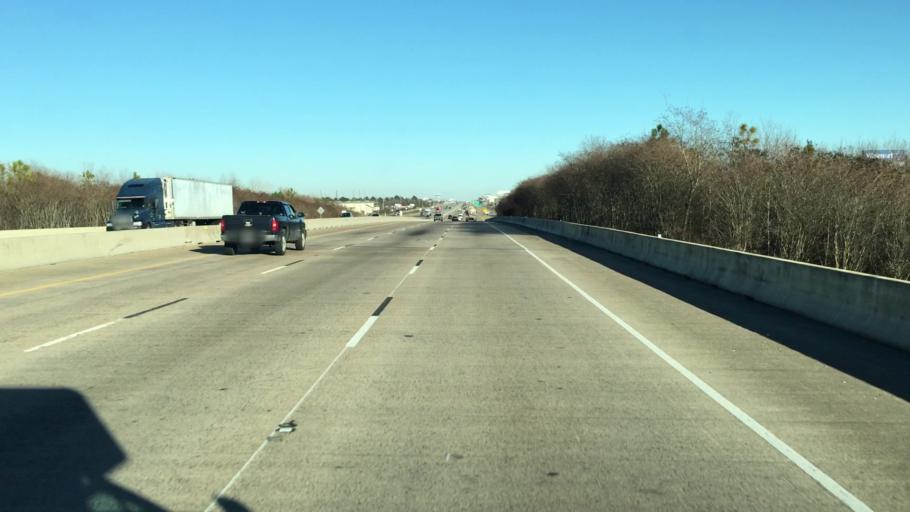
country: US
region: Texas
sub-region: Chambers County
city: Mont Belvieu
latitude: 29.8215
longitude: -94.8990
